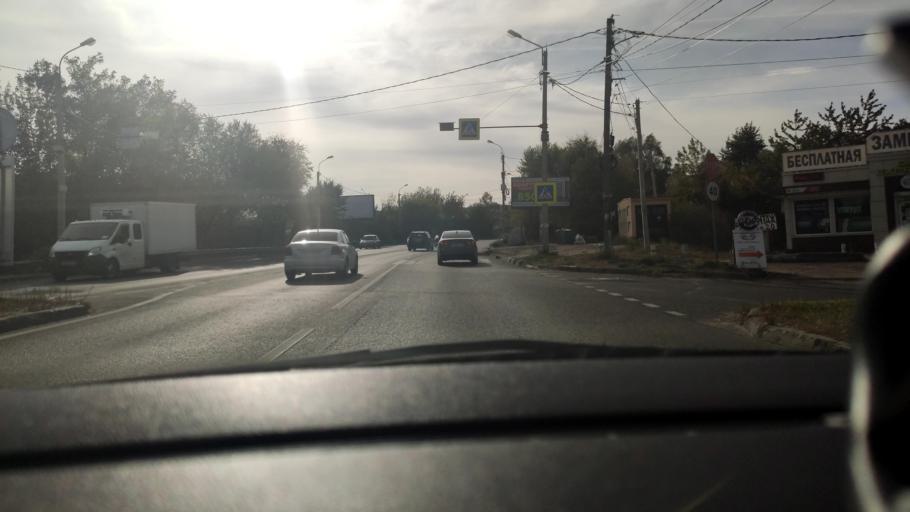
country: RU
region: Voronezj
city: Voronezh
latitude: 51.6940
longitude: 39.2191
